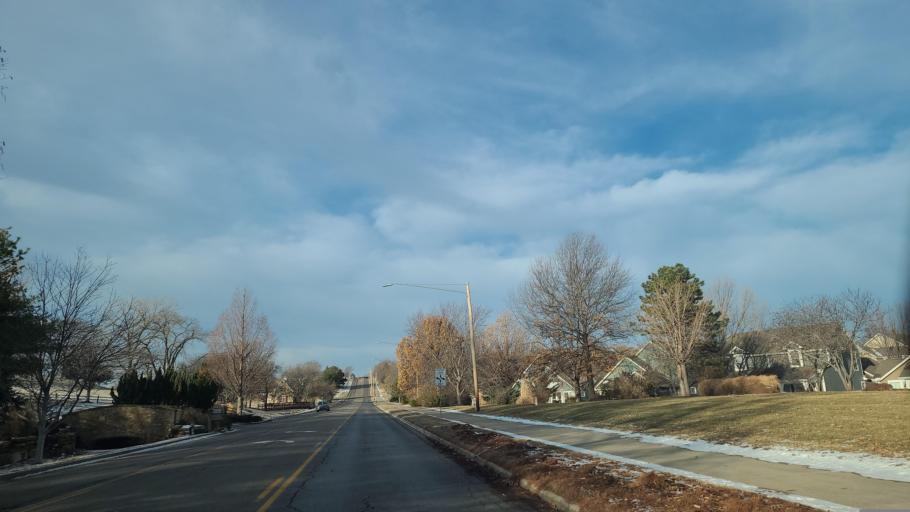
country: US
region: Kansas
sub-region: Douglas County
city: Lawrence
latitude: 38.9862
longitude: -95.2810
